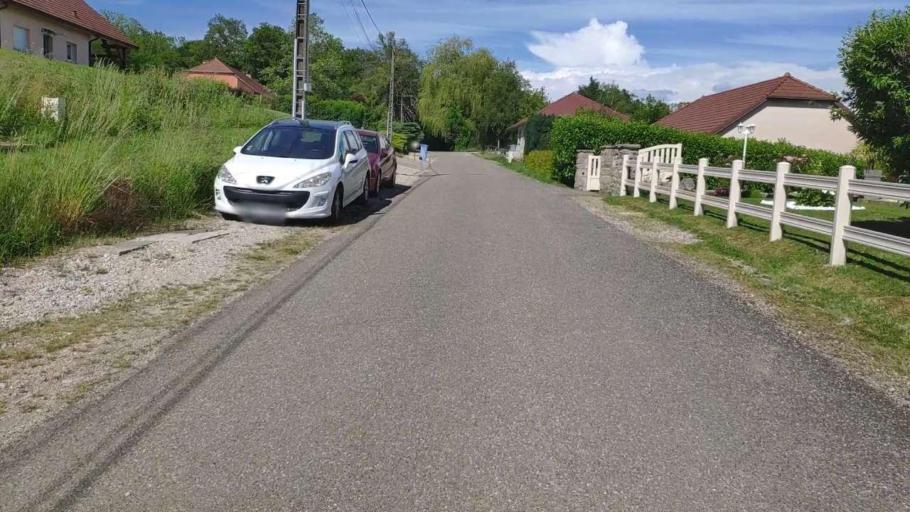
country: FR
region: Franche-Comte
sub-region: Departement du Jura
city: Bletterans
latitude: 46.7702
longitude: 5.4758
